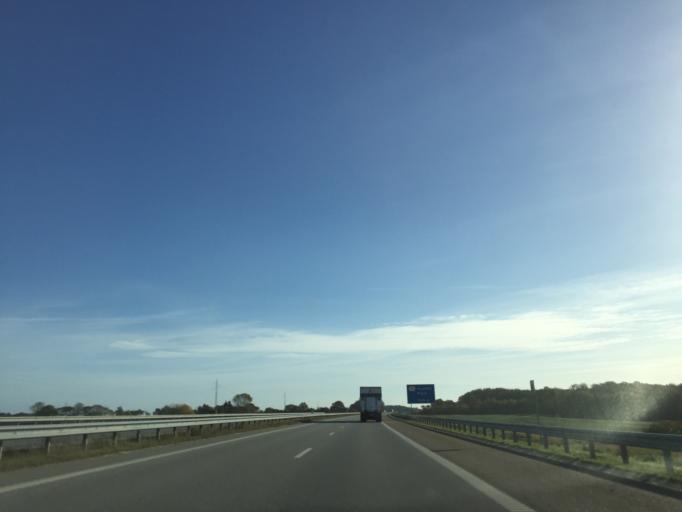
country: DK
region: South Denmark
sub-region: Sonderborg Kommune
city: Grasten
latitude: 54.9566
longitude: 9.6211
